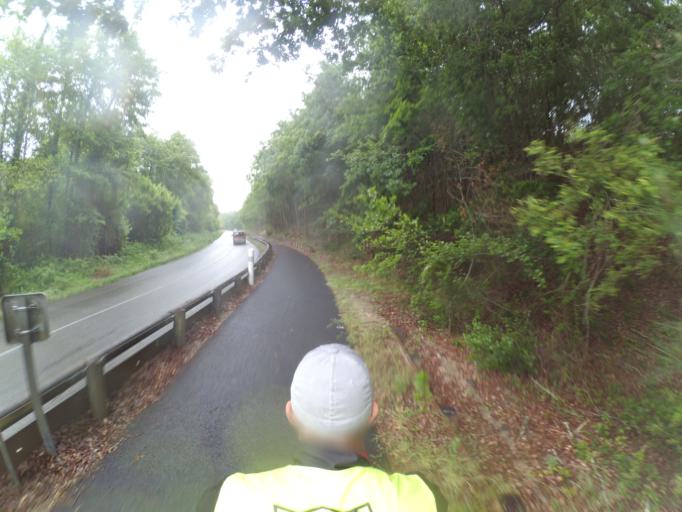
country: FR
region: Aquitaine
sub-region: Departement des Landes
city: Mimizan
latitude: 44.2335
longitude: -1.2238
